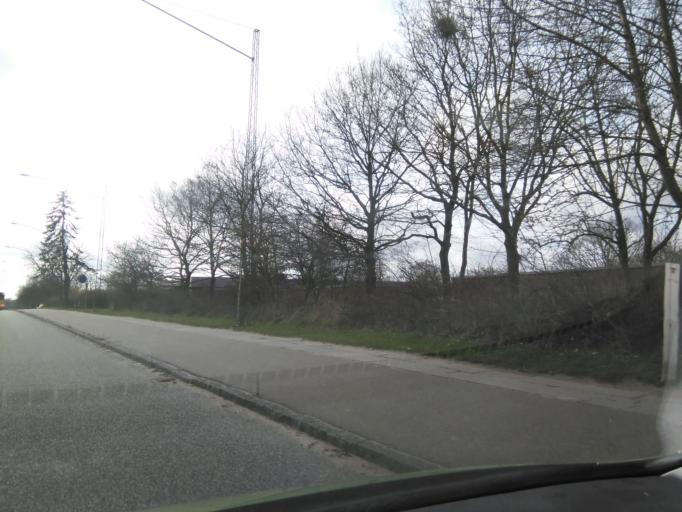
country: DK
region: Central Jutland
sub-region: Arhus Kommune
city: Arhus
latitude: 56.2005
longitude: 10.1876
